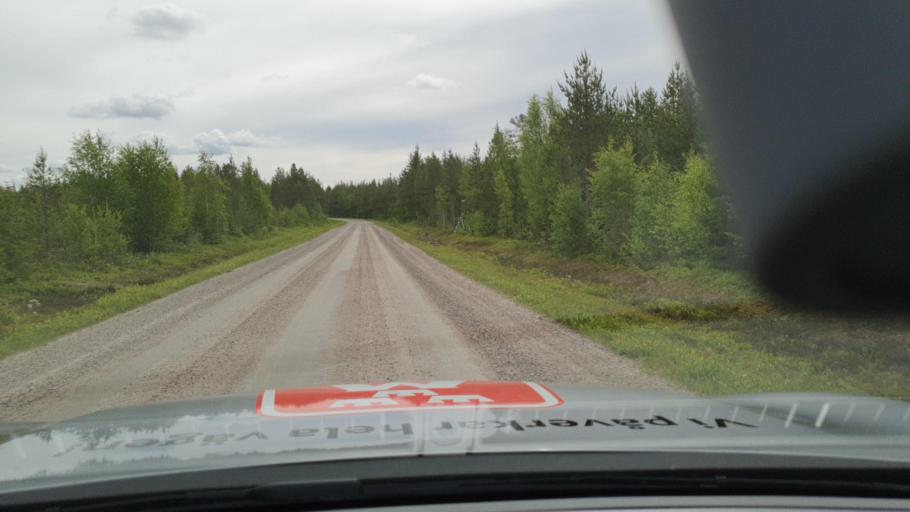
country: FI
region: Lapland
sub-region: Torniolaakso
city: Ylitornio
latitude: 65.9525
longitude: 23.7653
